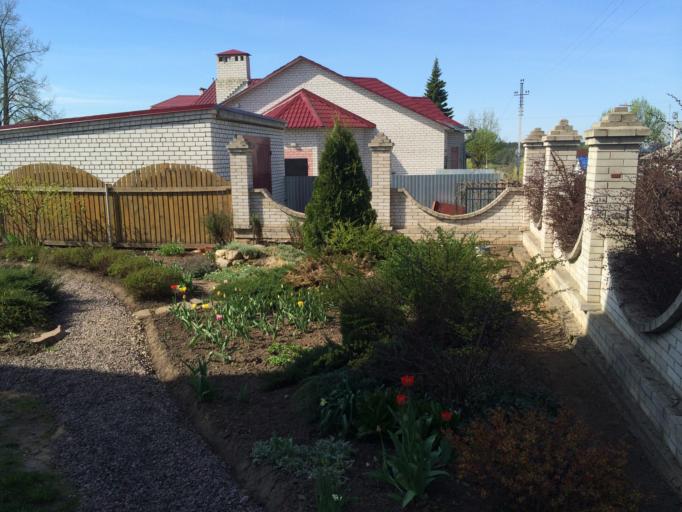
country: RU
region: Jaroslavl
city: Danilov
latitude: 58.1891
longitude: 40.1655
